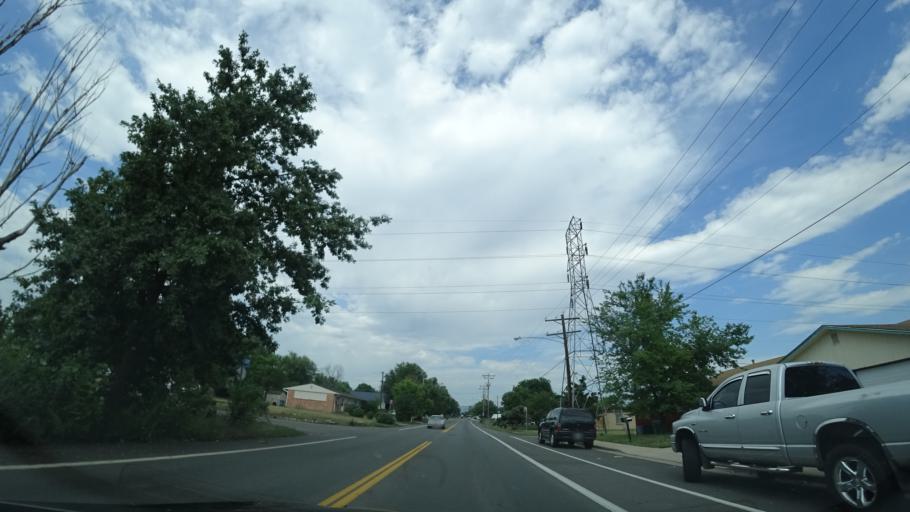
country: US
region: Colorado
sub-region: Jefferson County
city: Lakewood
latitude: 39.7186
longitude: -105.0599
